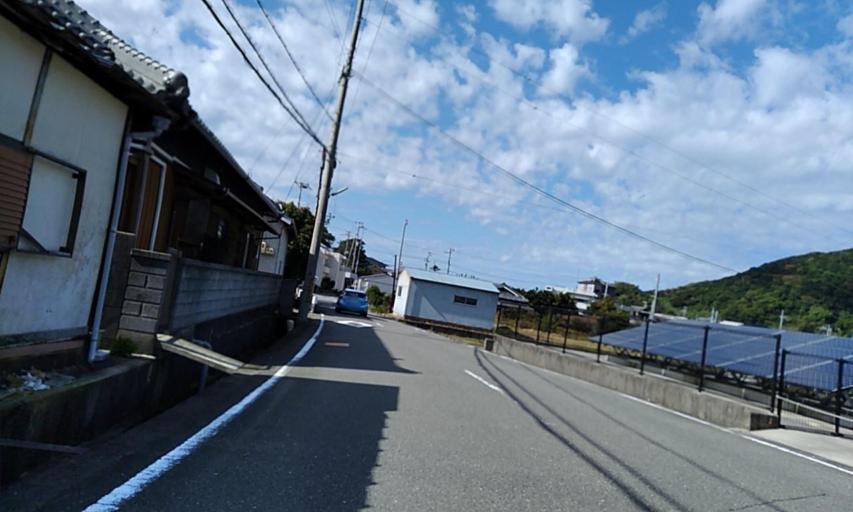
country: JP
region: Wakayama
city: Gobo
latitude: 33.9682
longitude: 135.0886
